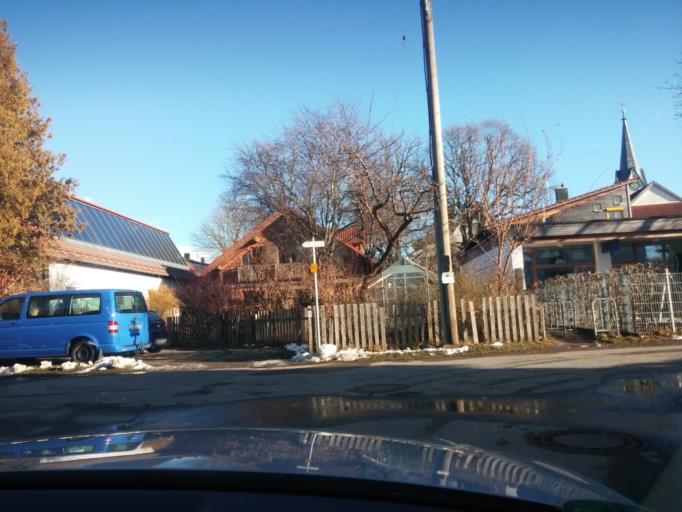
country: DE
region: Bavaria
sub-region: Swabia
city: Legau
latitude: 47.8572
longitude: 10.1282
